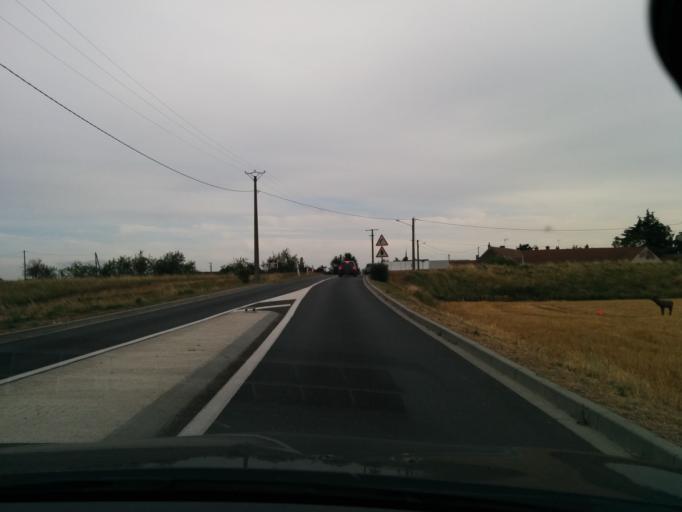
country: FR
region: Centre
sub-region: Departement du Loiret
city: Chateauneuf-sur-Loire
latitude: 47.8375
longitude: 2.2255
